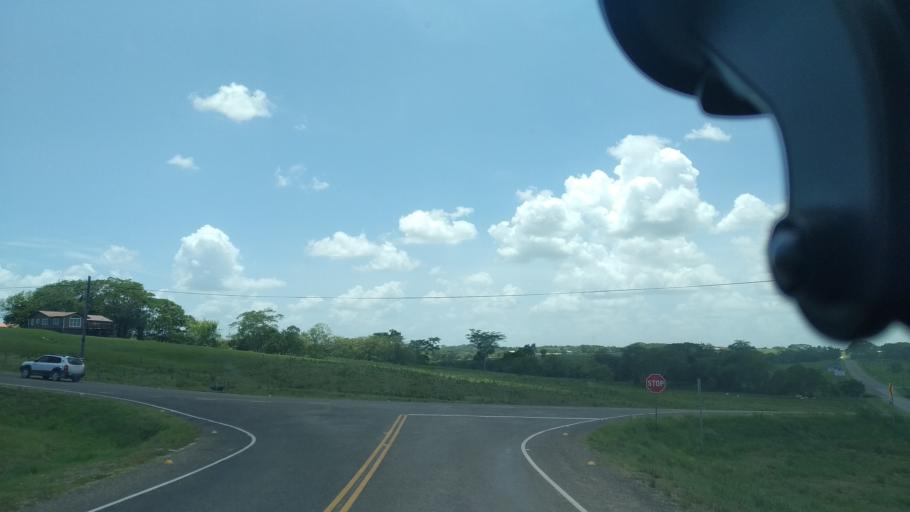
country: BZ
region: Cayo
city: San Ignacio
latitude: 17.2443
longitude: -88.9877
